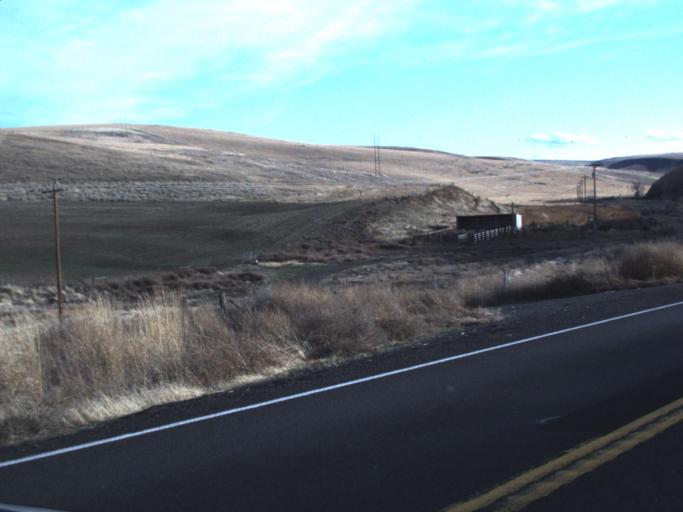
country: US
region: Washington
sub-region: Columbia County
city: Dayton
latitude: 46.4514
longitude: -117.9589
